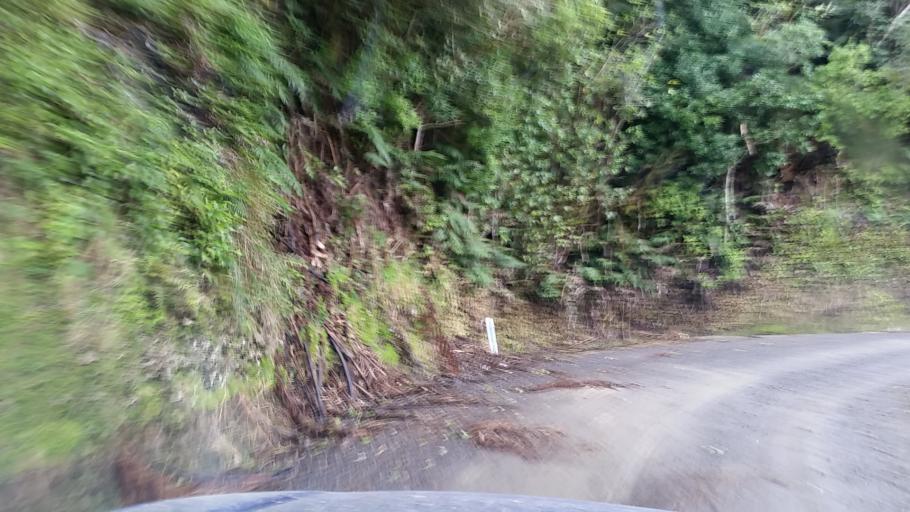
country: NZ
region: Taranaki
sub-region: South Taranaki District
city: Eltham
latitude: -39.1695
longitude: 174.6267
